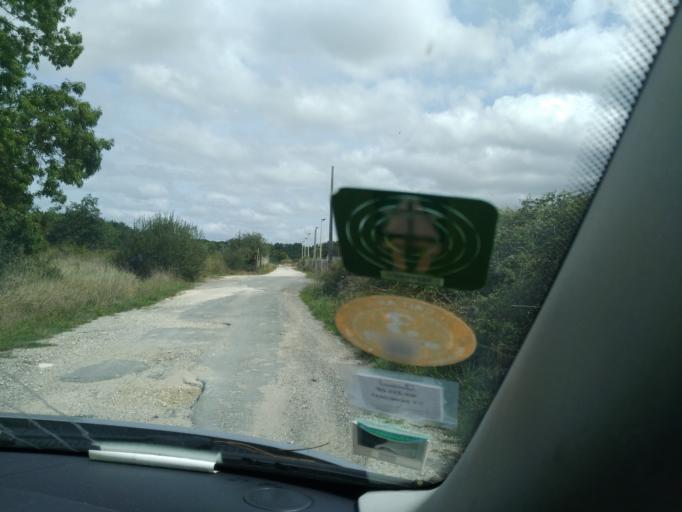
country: FR
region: Poitou-Charentes
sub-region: Departement de la Charente-Maritime
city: Chaillevette
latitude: 45.7134
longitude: -1.0724
